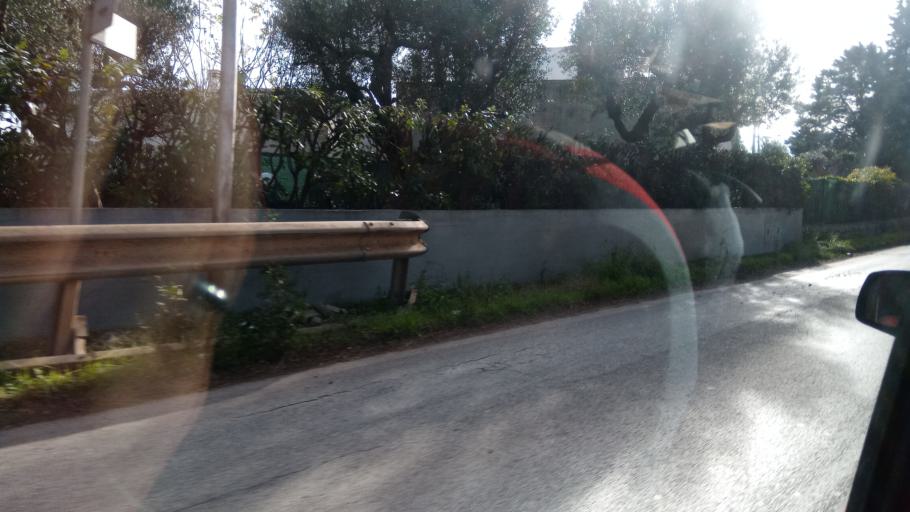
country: IT
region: Apulia
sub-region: Provincia di Bari
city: Castellana
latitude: 40.8956
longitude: 17.1658
